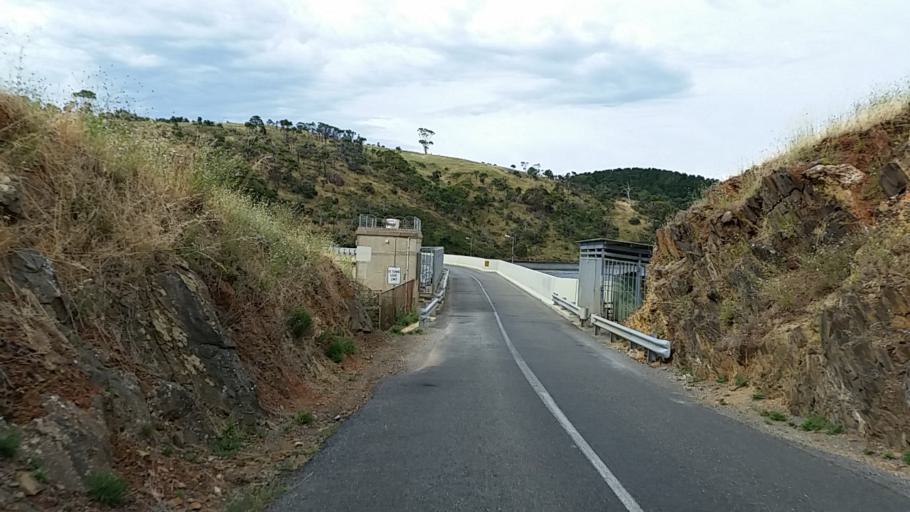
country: AU
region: South Australia
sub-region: Yankalilla
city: Normanville
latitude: -35.4016
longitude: 138.4196
